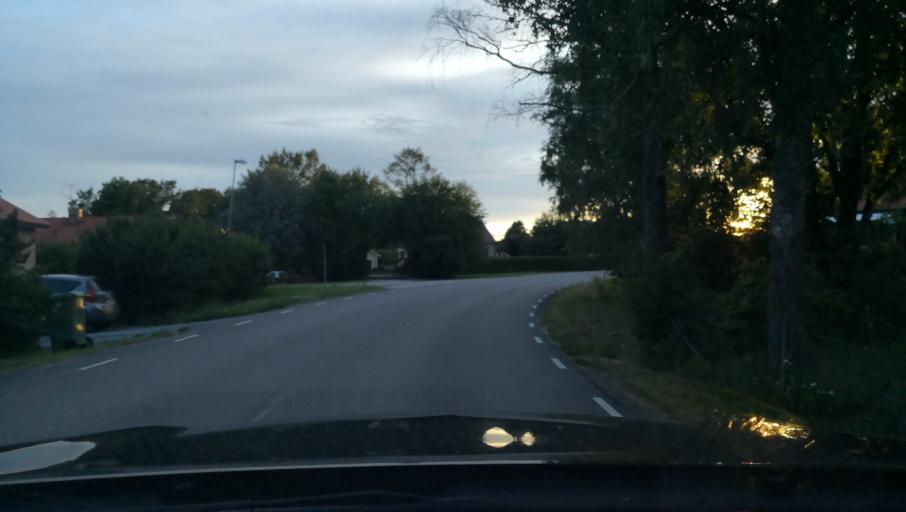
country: SE
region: Uppsala
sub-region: Enkopings Kommun
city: Grillby
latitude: 59.6594
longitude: 17.2433
